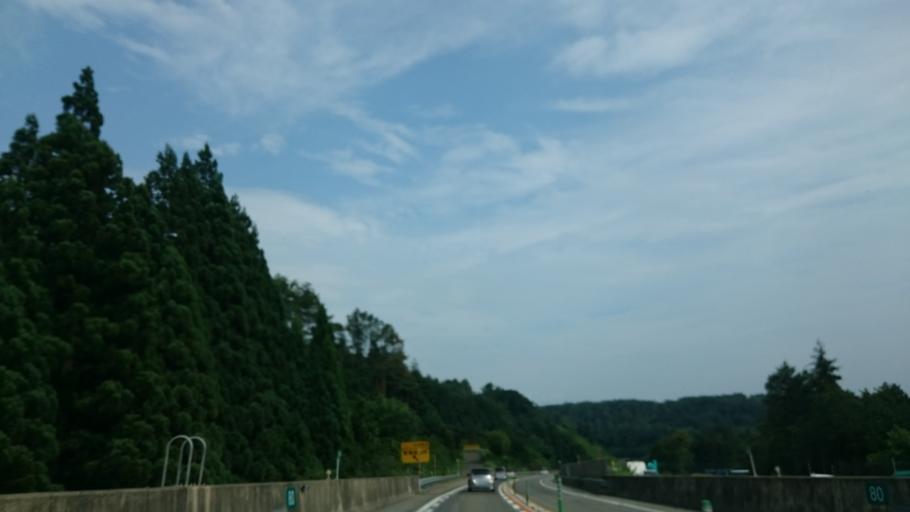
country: JP
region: Gifu
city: Gujo
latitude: 35.9018
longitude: 136.8759
